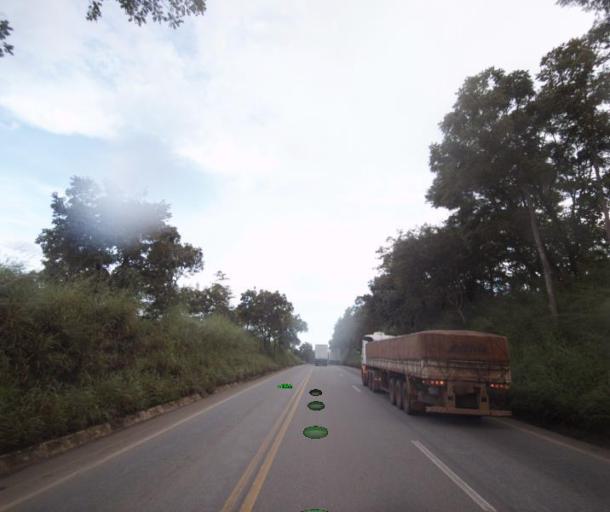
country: BR
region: Goias
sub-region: Porangatu
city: Porangatu
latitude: -13.9690
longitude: -49.0903
